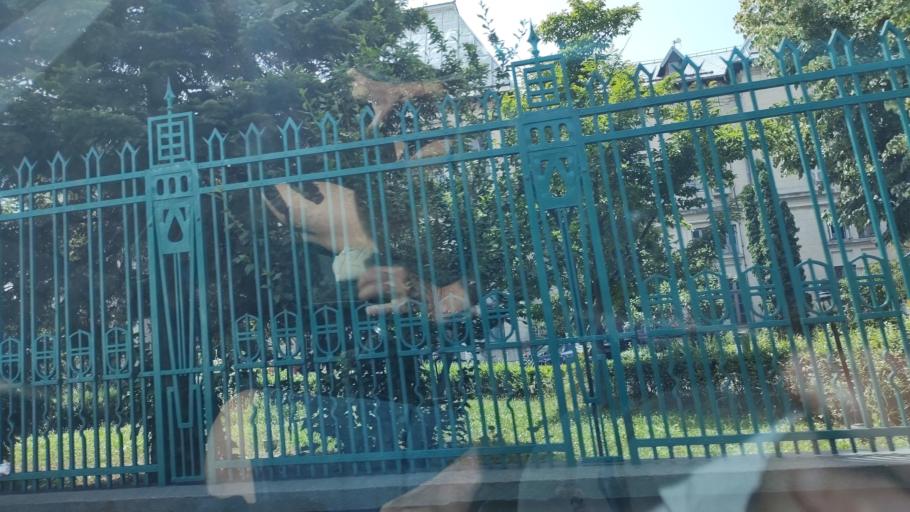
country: RO
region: Mehedinti
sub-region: Municipiul Drobeta-Turnu Severin
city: Drobeta-Turnu Severin
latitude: 44.6246
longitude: 22.6618
